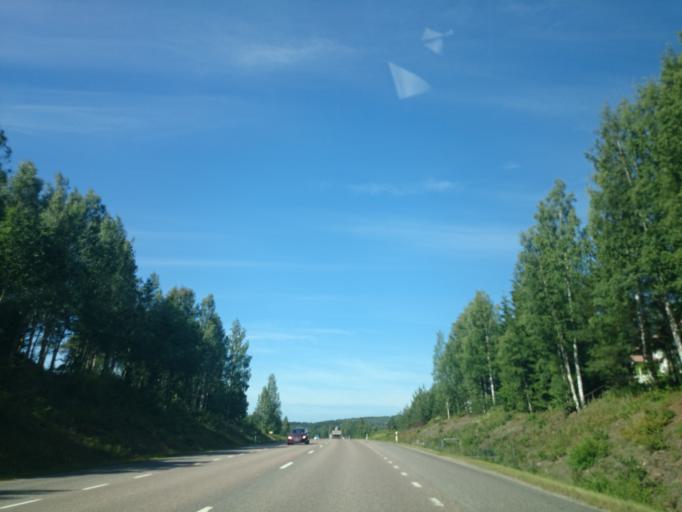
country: SE
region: Vaesternorrland
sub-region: Sundsvalls Kommun
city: Vi
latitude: 62.3762
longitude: 17.1267
